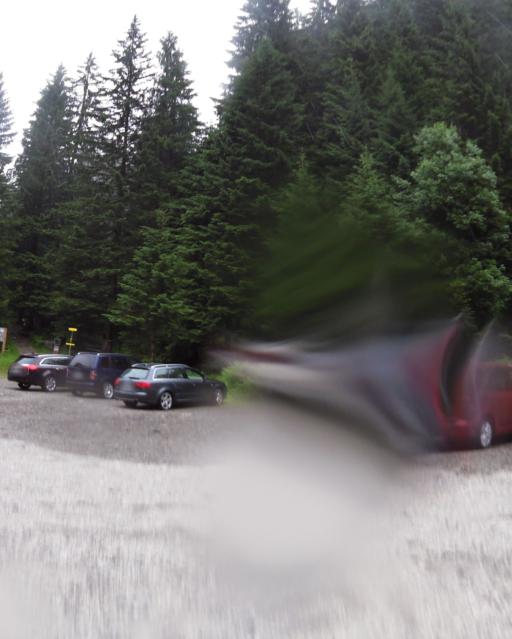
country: AT
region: Tyrol
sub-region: Politischer Bezirk Innsbruck Land
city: Neustift im Stubaital
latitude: 47.0263
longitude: 11.2220
